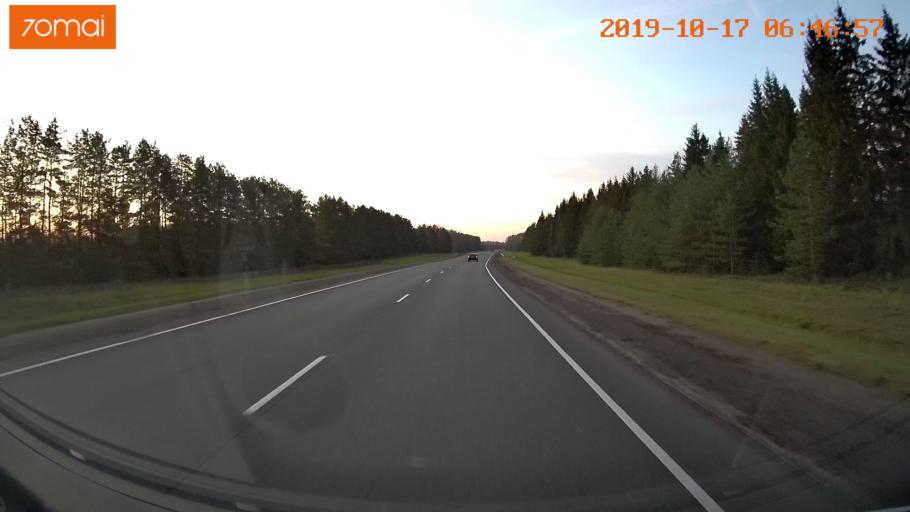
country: RU
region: Vladimir
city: Kideksha
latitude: 56.5428
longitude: 40.5545
